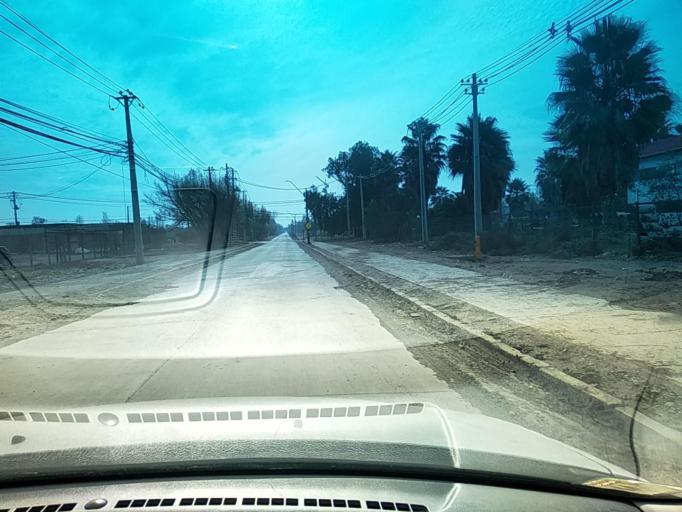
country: CL
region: Santiago Metropolitan
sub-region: Provincia de Chacabuco
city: Chicureo Abajo
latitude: -33.3109
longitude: -70.7145
